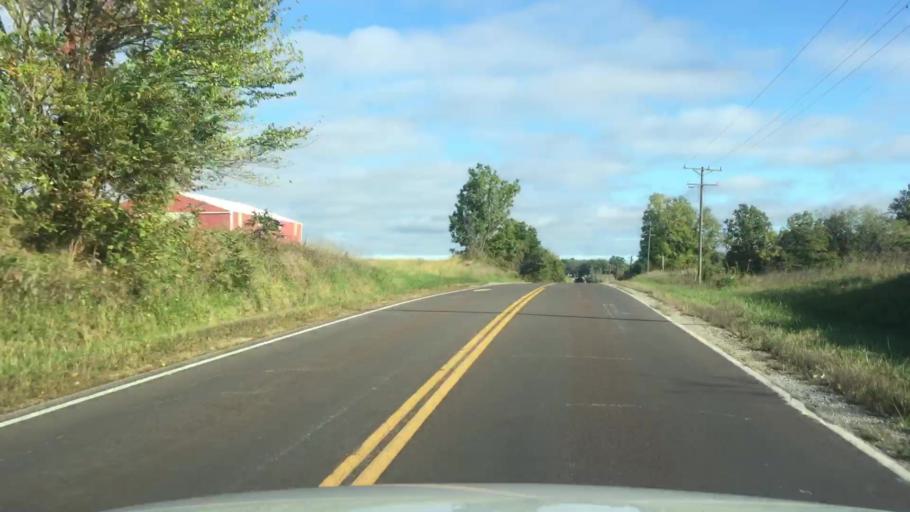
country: US
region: Missouri
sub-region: Howard County
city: New Franklin
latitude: 39.0524
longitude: -92.7444
